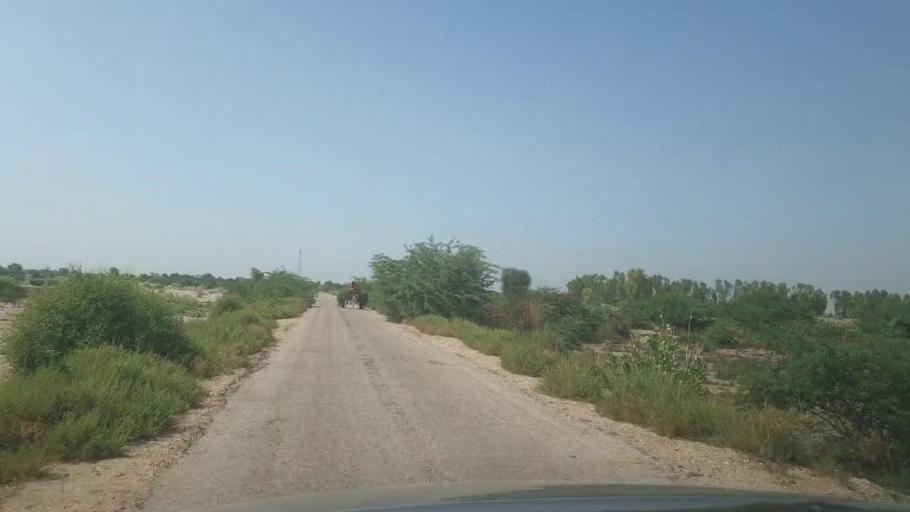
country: PK
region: Sindh
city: Rohri
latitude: 27.4152
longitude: 69.0801
